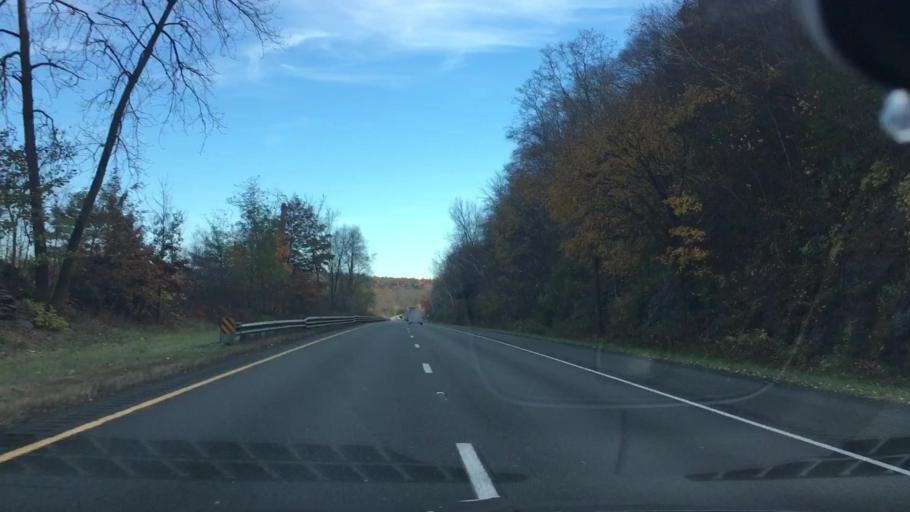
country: US
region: Massachusetts
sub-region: Hampshire County
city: Northampton
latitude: 42.2841
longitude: -72.6156
